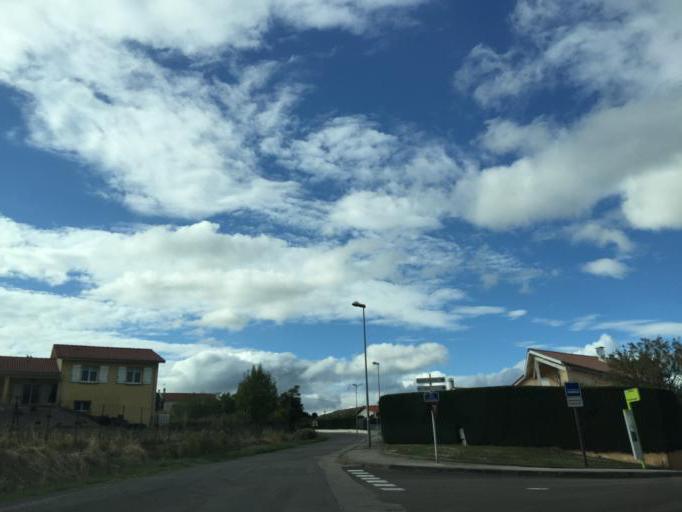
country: FR
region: Rhone-Alpes
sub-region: Departement de la Loire
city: La Grand-Croix
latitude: 45.5029
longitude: 4.5506
